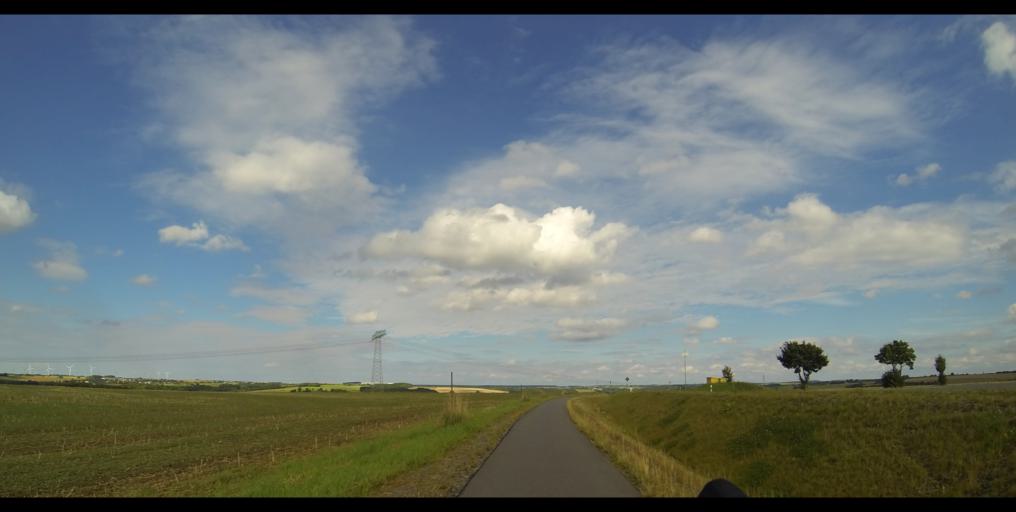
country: DE
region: Saxony
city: Hainichen
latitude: 50.9892
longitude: 13.1570
